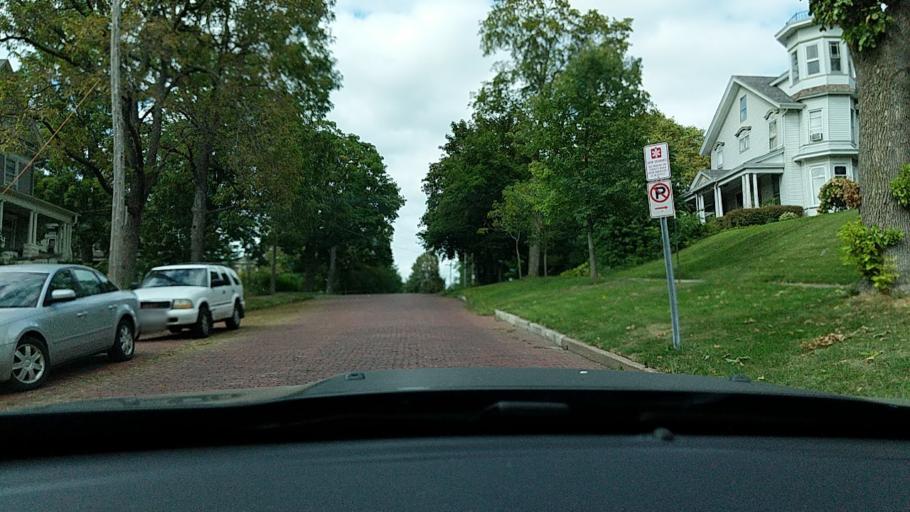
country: US
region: Iowa
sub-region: Scott County
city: Davenport
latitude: 41.5307
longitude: -90.5538
